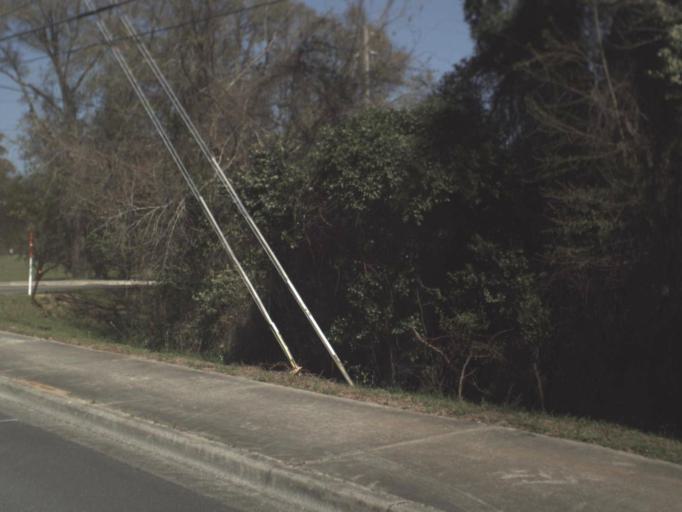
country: US
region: Florida
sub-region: Leon County
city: Tallahassee
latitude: 30.4018
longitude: -84.2805
